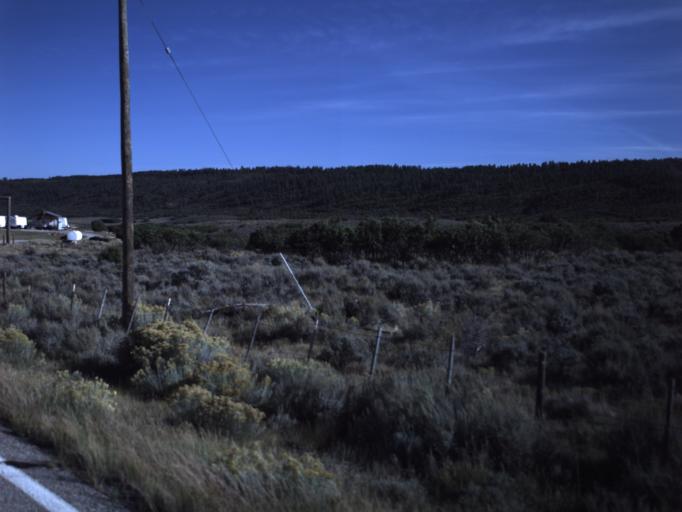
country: US
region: Utah
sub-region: Grand County
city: Moab
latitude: 38.3383
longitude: -109.1649
